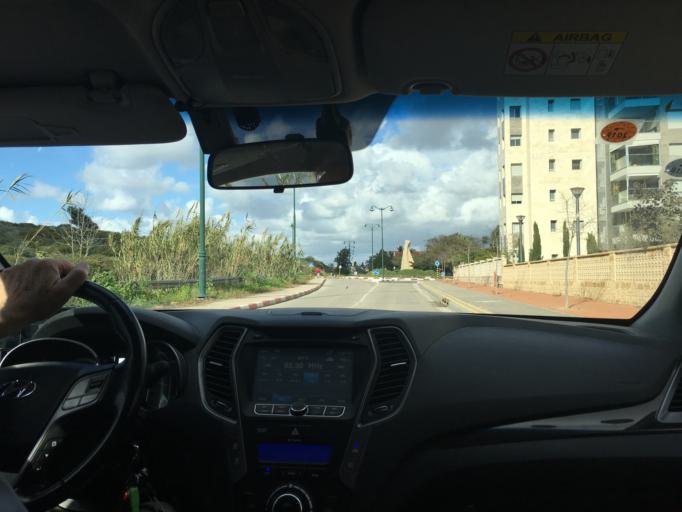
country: IL
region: Central District
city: Ness Ziona
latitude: 31.9319
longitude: 34.7860
